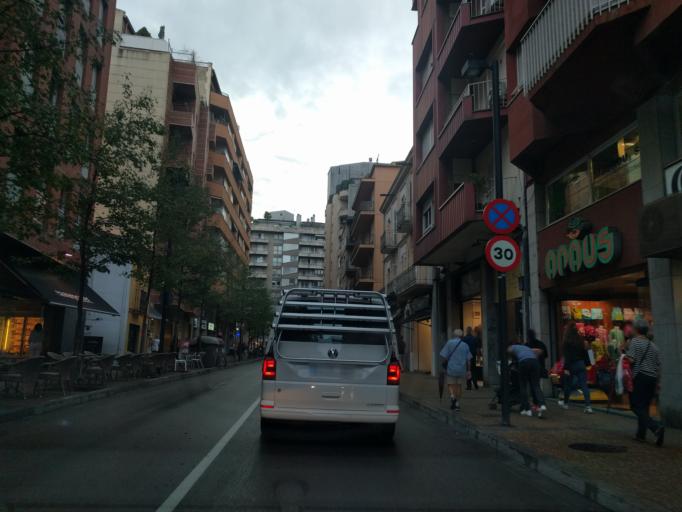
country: ES
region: Catalonia
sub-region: Provincia de Girona
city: Girona
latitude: 41.9768
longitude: 2.8209
